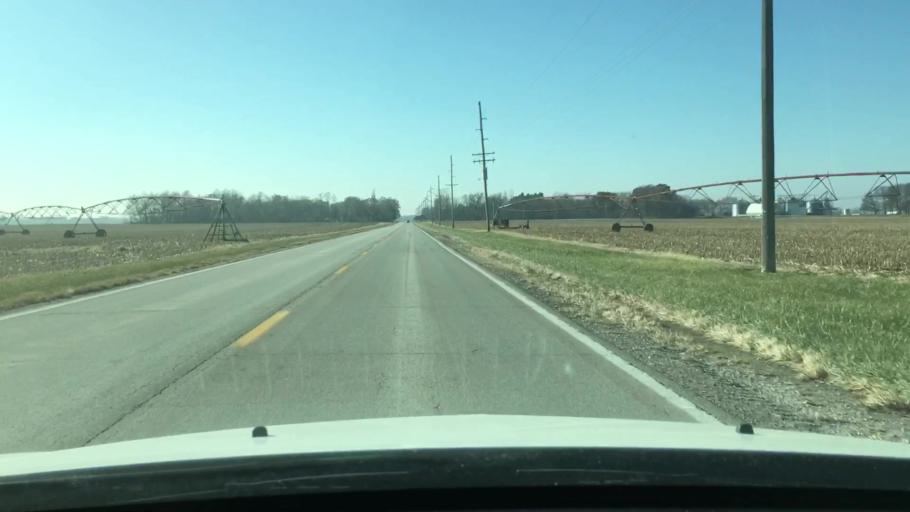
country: US
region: Illinois
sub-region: Cass County
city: Beardstown
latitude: 39.9749
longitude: -90.4588
